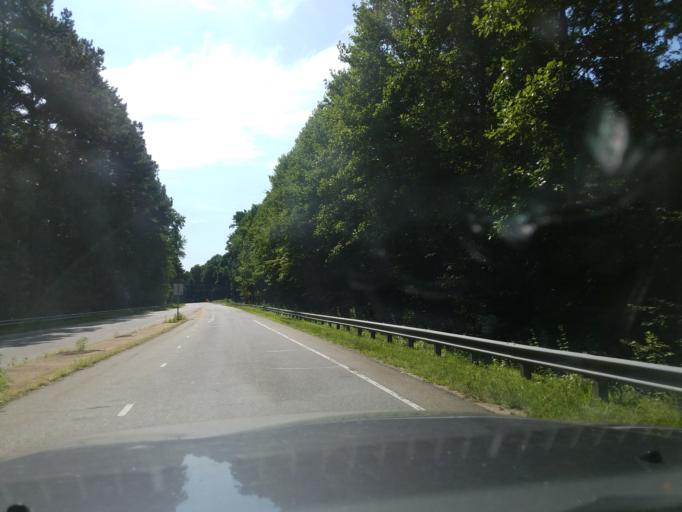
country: US
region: North Carolina
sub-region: Granville County
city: Oxford
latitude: 36.3139
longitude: -78.5393
